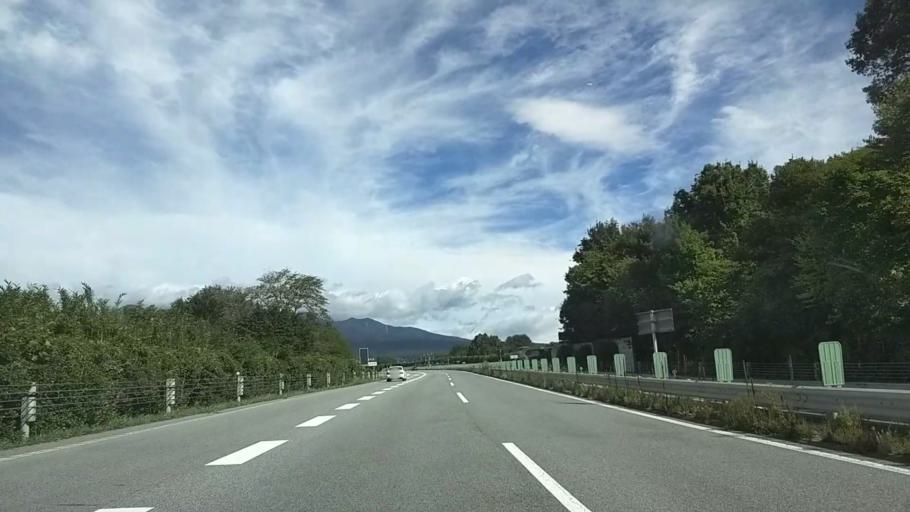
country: JP
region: Yamanashi
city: Nirasaki
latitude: 35.8280
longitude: 138.3924
